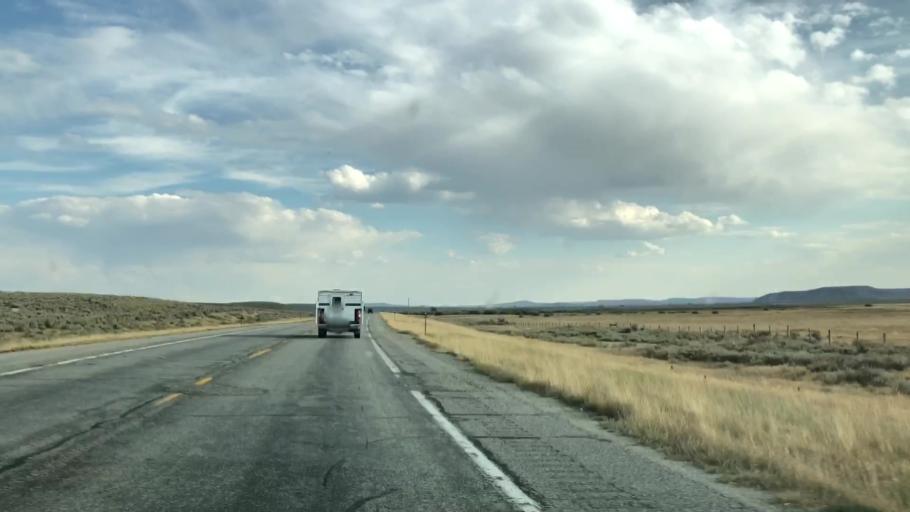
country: US
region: Wyoming
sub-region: Sublette County
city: Pinedale
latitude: 43.0300
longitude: -110.1270
